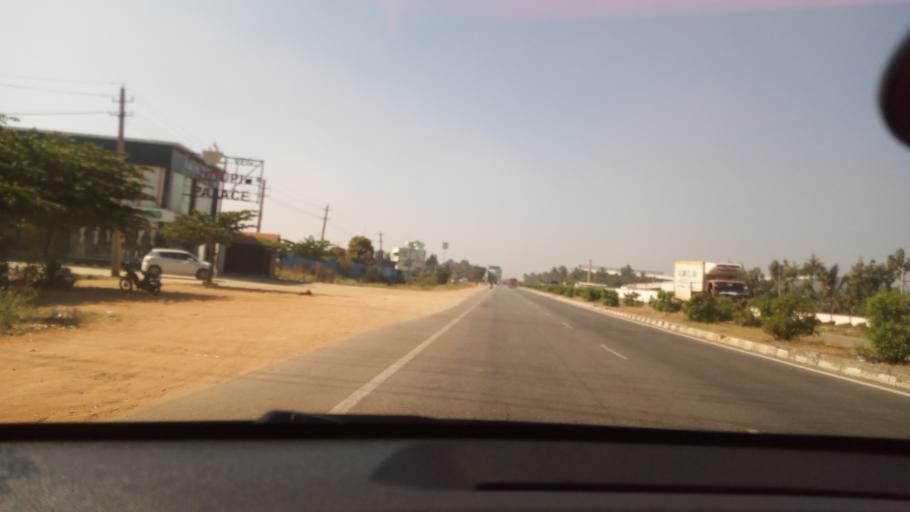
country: IN
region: Karnataka
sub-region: Bangalore Rural
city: Nelamangala
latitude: 13.0780
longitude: 77.3668
